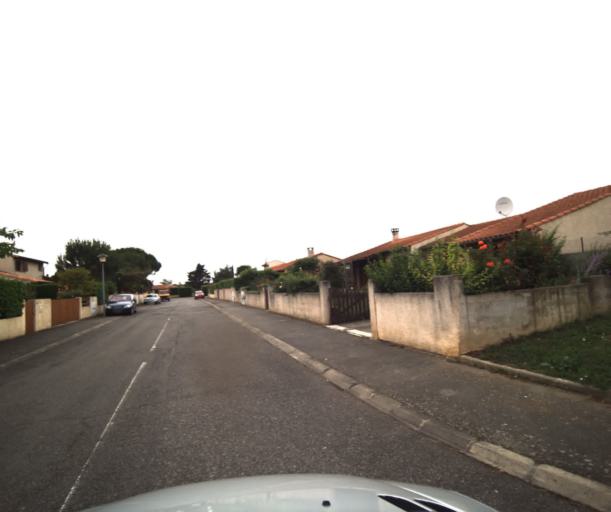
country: FR
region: Midi-Pyrenees
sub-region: Departement de la Haute-Garonne
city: Labarthe-sur-Leze
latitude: 43.4444
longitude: 1.3961
